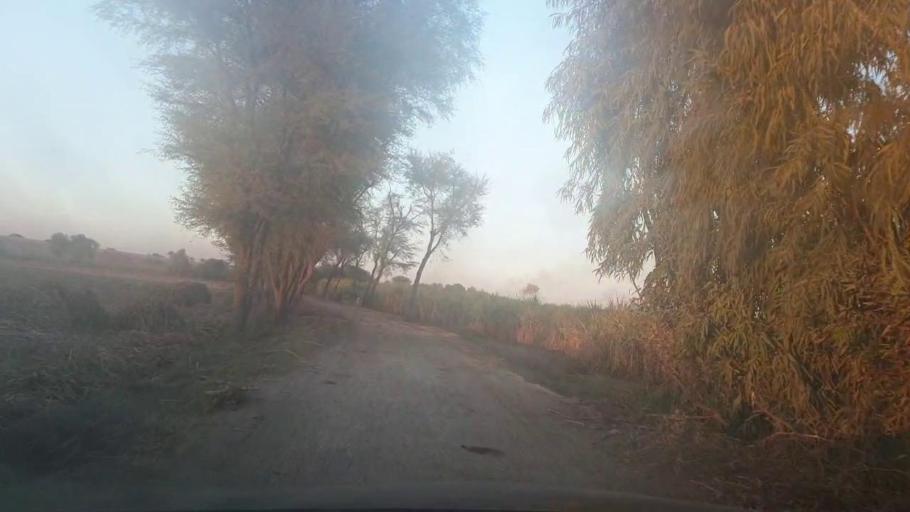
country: PK
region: Sindh
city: Ghotki
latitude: 28.0570
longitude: 69.3674
